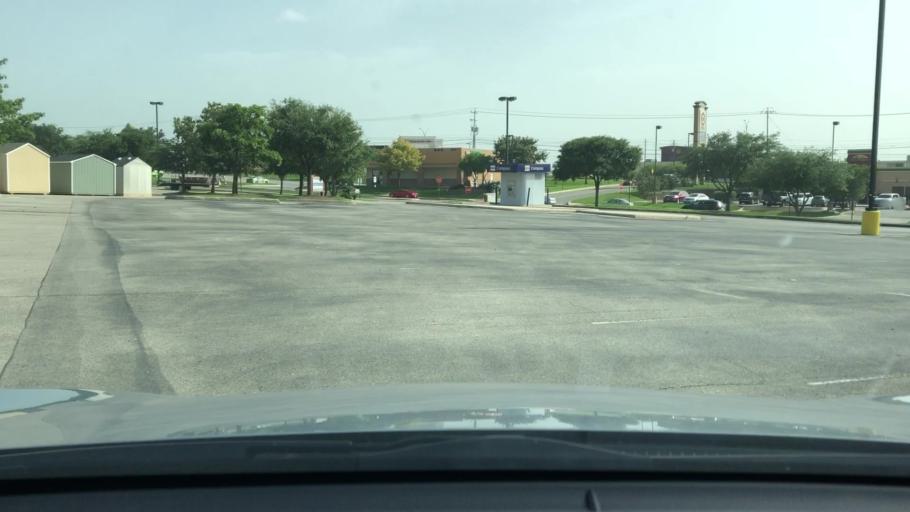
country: US
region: Texas
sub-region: Bexar County
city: Live Oak
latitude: 29.5665
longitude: -98.3292
